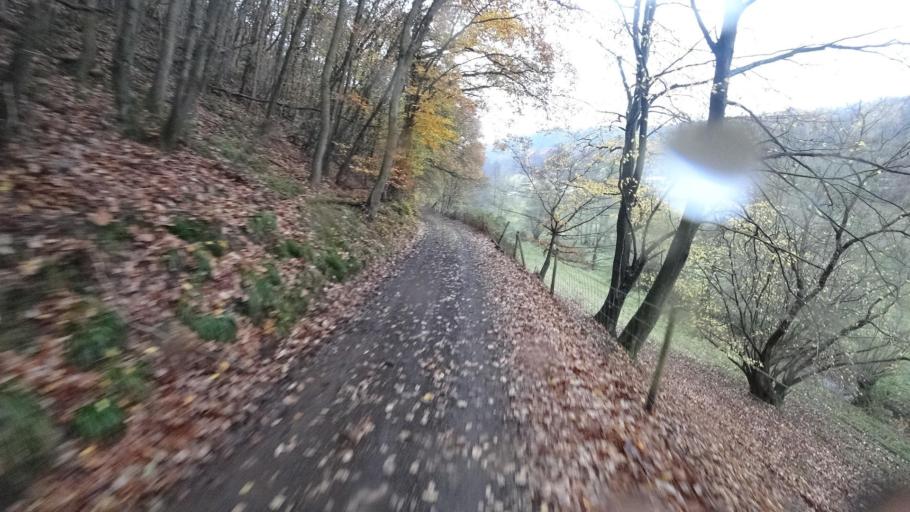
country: DE
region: Rheinland-Pfalz
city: Bad Neuenahr-Ahrweiler
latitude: 50.5249
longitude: 7.0924
